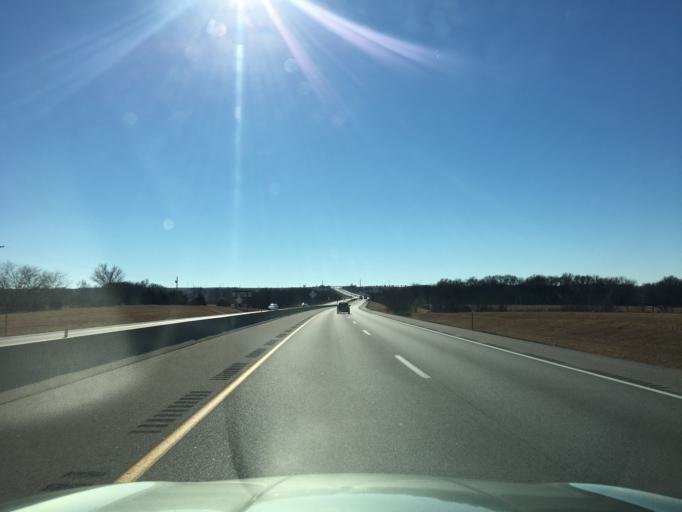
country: US
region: Kansas
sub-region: Sumner County
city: Wellington
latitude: 37.2212
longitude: -97.3388
